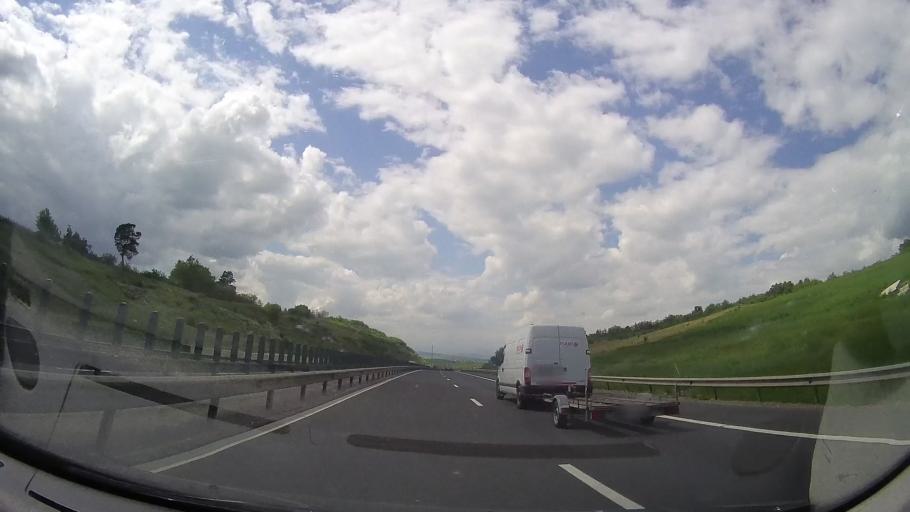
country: RO
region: Sibiu
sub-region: Oras Saliste
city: Saliste
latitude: 45.8181
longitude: 23.8770
